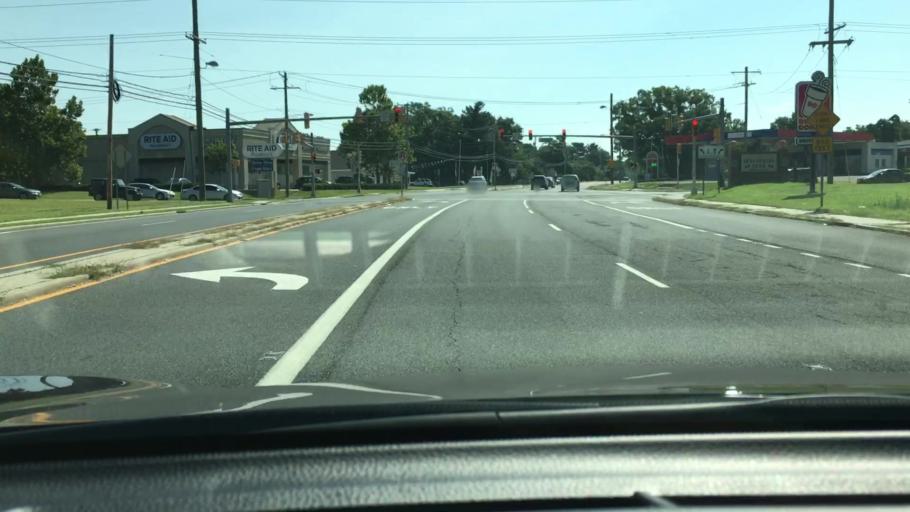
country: US
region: New Jersey
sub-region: Cumberland County
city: Millville
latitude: 39.3948
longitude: -75.0192
